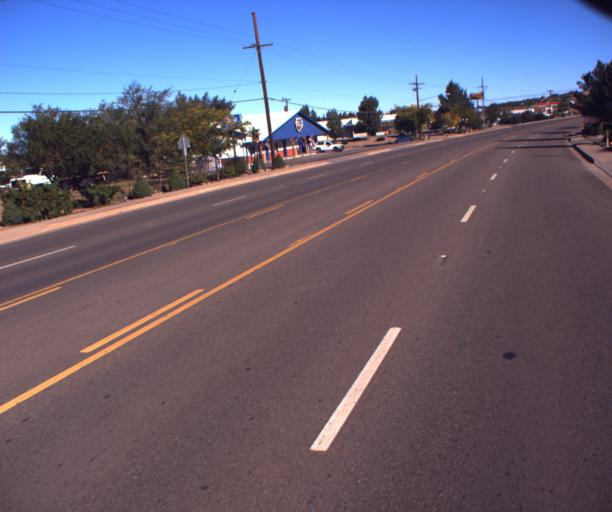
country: US
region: Arizona
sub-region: Navajo County
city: Taylor
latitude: 34.4667
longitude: -110.0912
